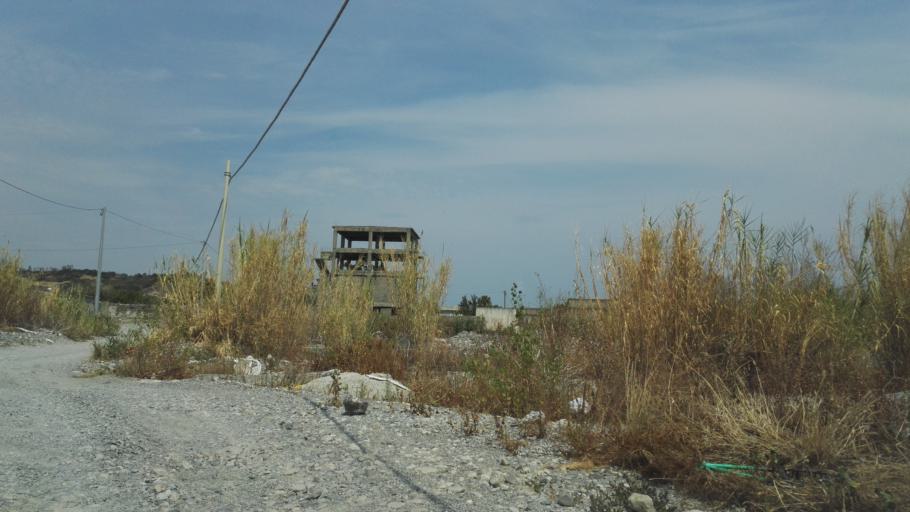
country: IT
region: Calabria
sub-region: Provincia di Reggio Calabria
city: Monasterace Marina
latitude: 38.4272
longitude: 16.5675
